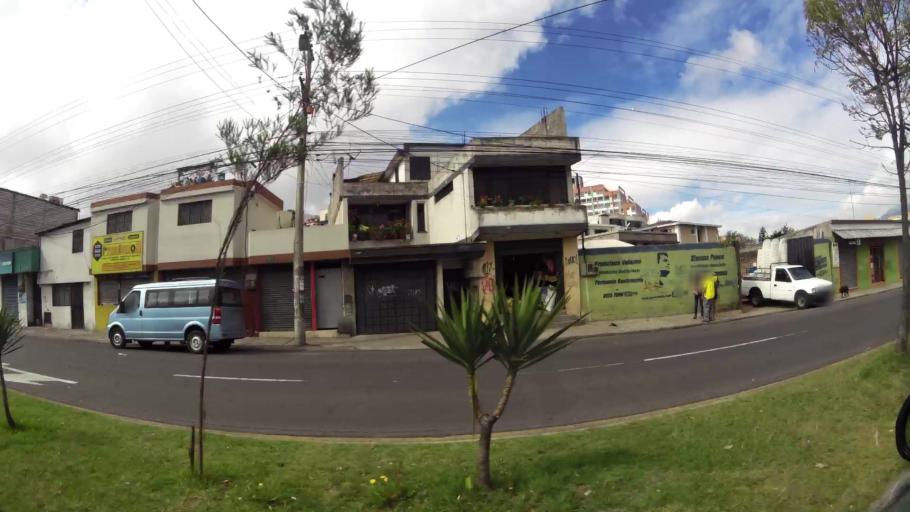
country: EC
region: Pichincha
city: Quito
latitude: -0.1538
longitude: -78.4682
